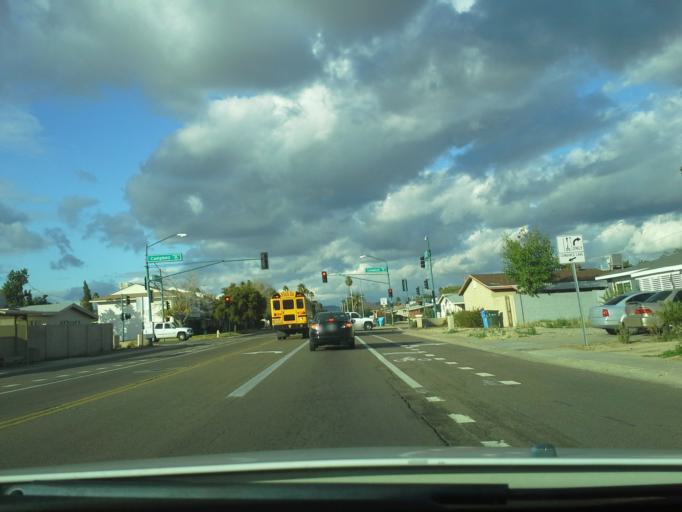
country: US
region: Arizona
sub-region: Maricopa County
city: Phoenix
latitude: 33.5015
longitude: -112.0913
